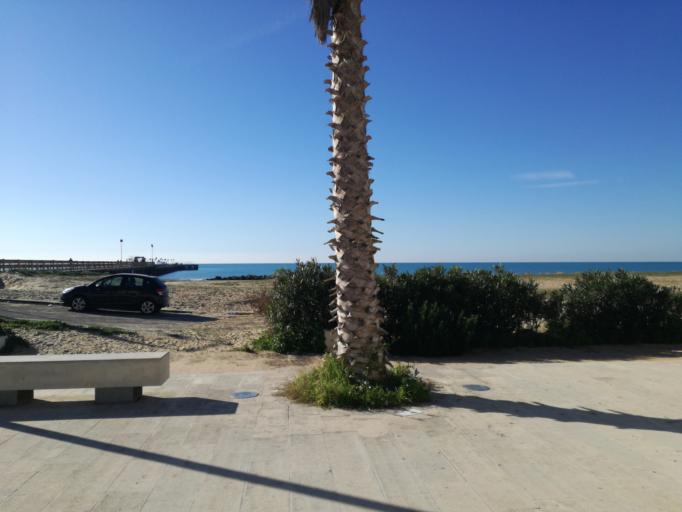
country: IT
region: Sicily
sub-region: Provincia di Caltanissetta
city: Gela
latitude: 37.0644
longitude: 14.2471
